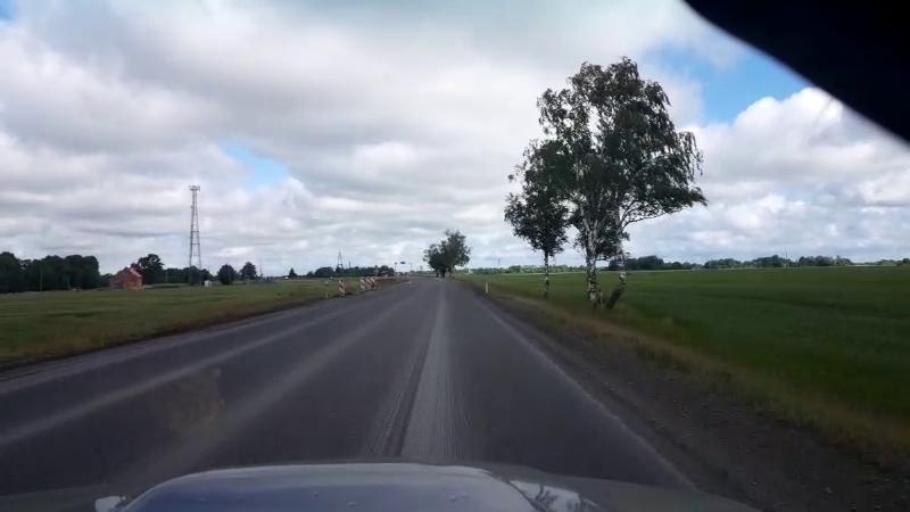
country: LV
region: Bauskas Rajons
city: Bauska
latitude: 56.2890
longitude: 24.3558
